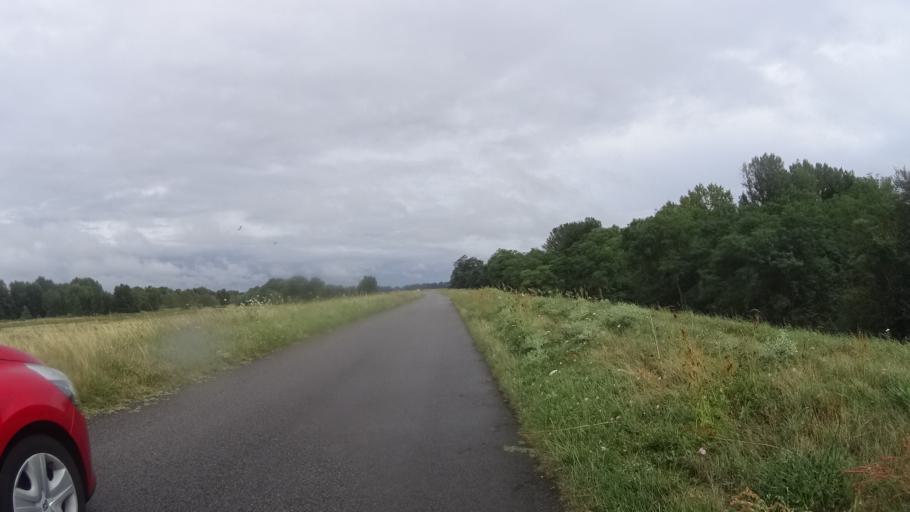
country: FR
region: Centre
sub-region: Departement du Loiret
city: Checy
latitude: 47.8847
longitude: 2.0055
